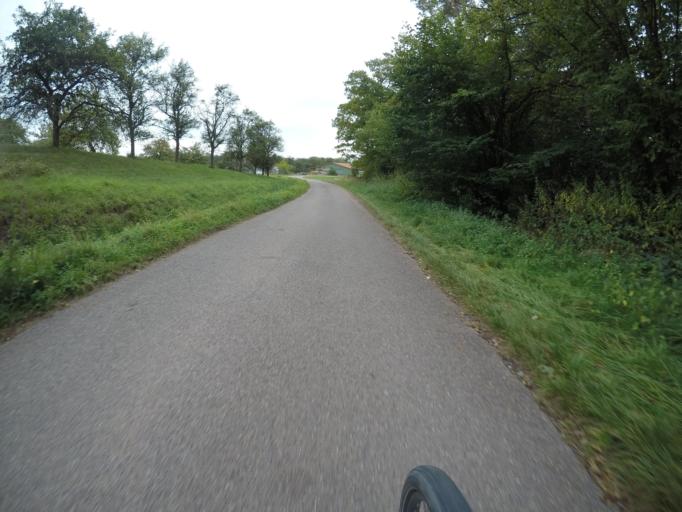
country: DE
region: Baden-Wuerttemberg
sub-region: Karlsruhe Region
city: Maulbronn
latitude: 48.9925
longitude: 8.8489
